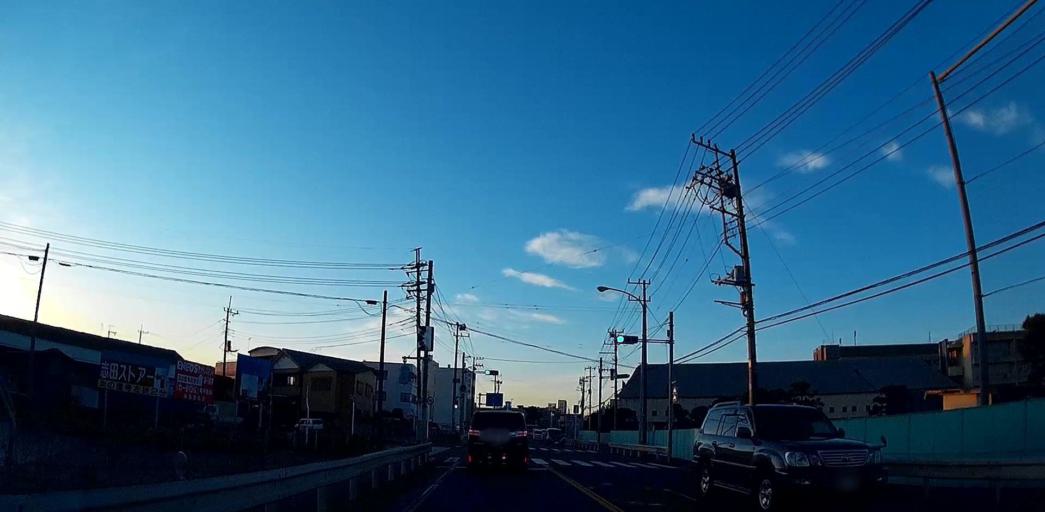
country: JP
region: Chiba
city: Katori-shi
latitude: 35.8958
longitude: 140.5007
